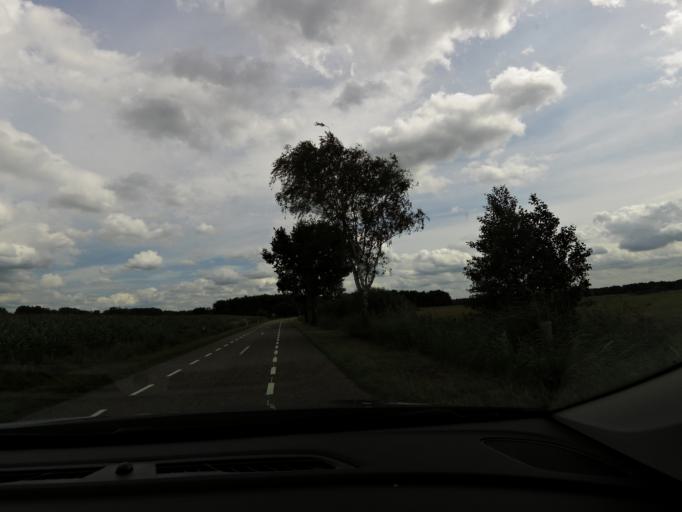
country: BE
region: Flanders
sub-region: Provincie Antwerpen
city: Hoogstraten
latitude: 51.4201
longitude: 4.8144
